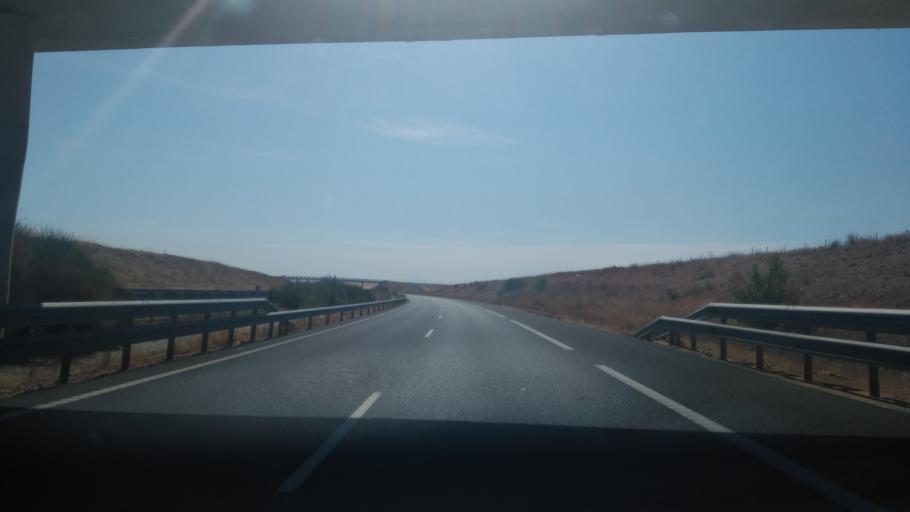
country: ES
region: Castille and Leon
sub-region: Provincia de Salamanca
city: Machacon
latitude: 40.9215
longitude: -5.5318
